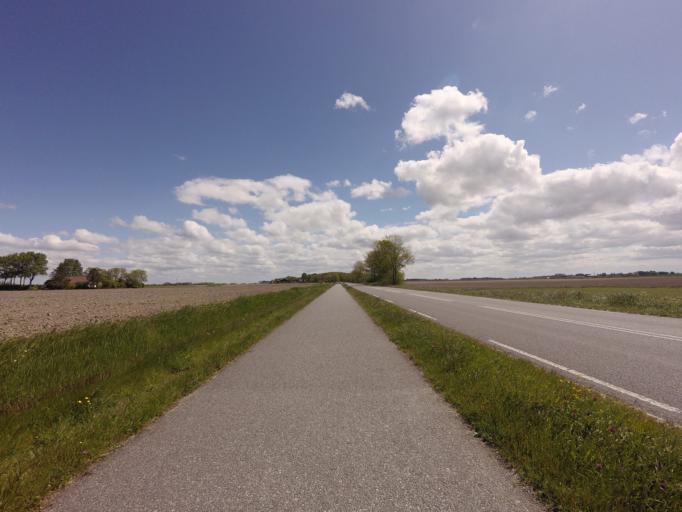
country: NL
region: Friesland
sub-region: Gemeente Harlingen
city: Harlingen
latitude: 53.1393
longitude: 5.4461
